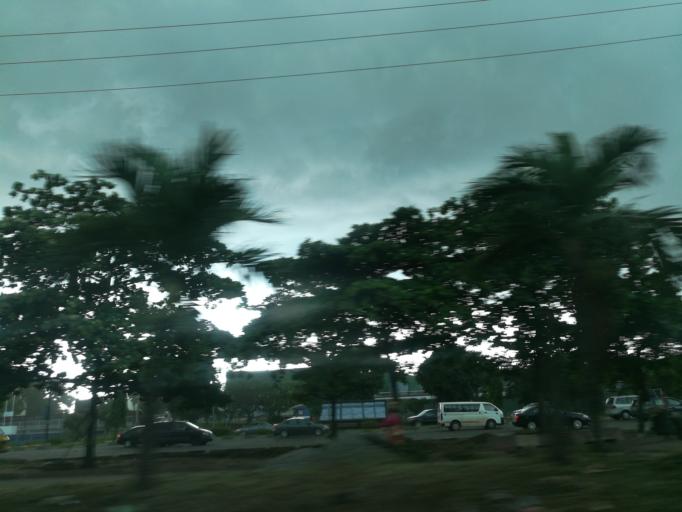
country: NG
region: Lagos
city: Ojota
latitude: 6.6016
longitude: 3.3772
